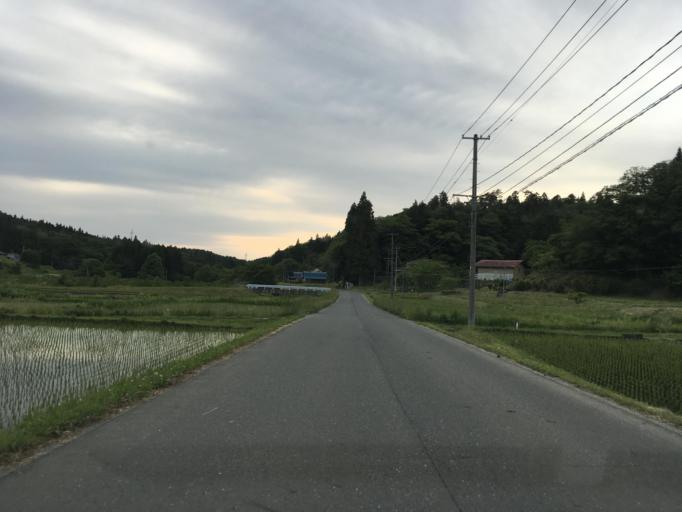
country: JP
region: Iwate
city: Mizusawa
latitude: 39.1640
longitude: 141.3100
